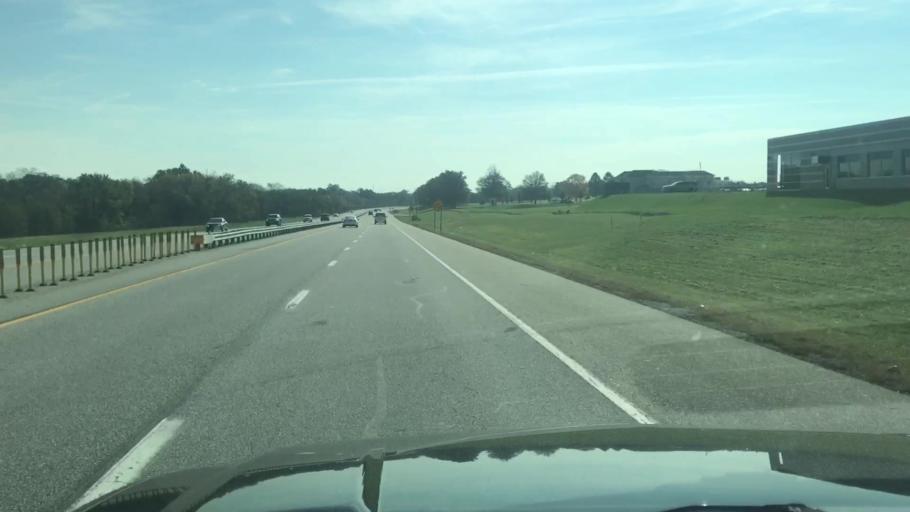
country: US
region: Pennsylvania
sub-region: Cumberland County
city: Mechanicsburg
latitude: 40.2613
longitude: -77.0394
